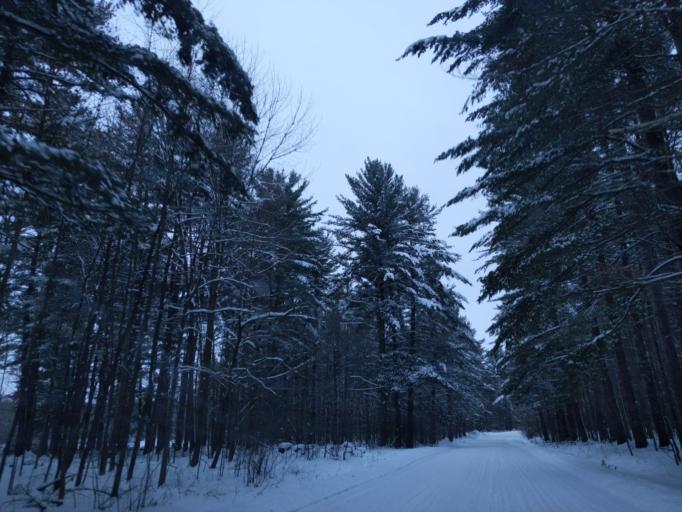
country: US
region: Wisconsin
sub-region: Marathon County
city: Marathon
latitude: 44.7684
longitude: -89.8695
